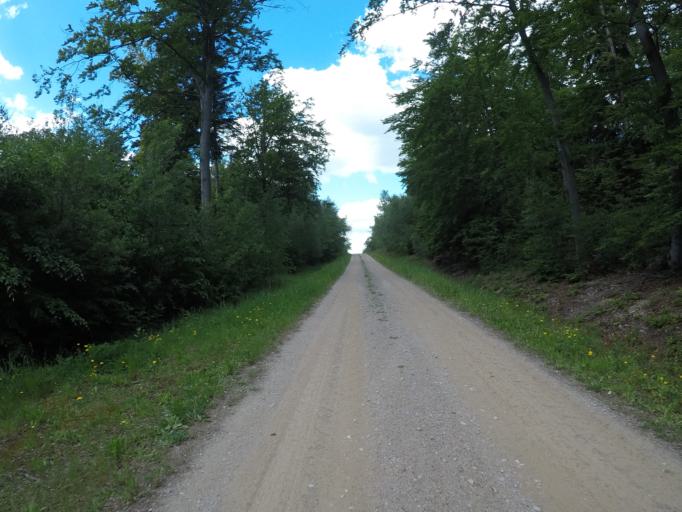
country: PL
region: Swietokrzyskie
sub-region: Powiat kielecki
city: Kostomloty Pierwsze
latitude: 50.9335
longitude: 20.6214
